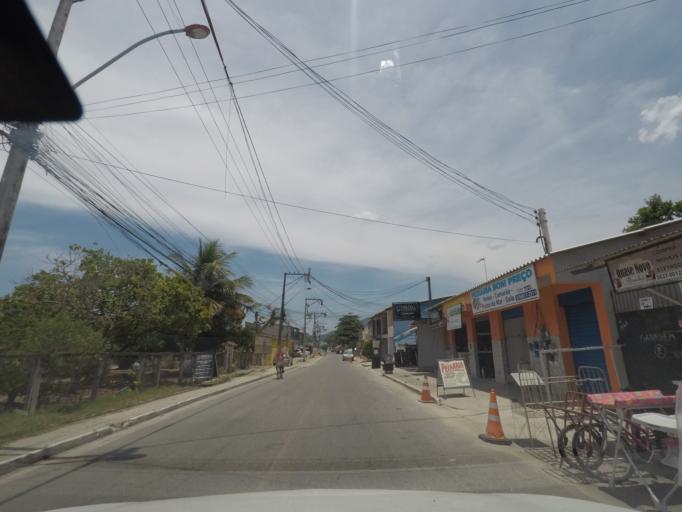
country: BR
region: Rio de Janeiro
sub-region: Marica
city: Marica
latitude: -22.9094
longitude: -42.8302
